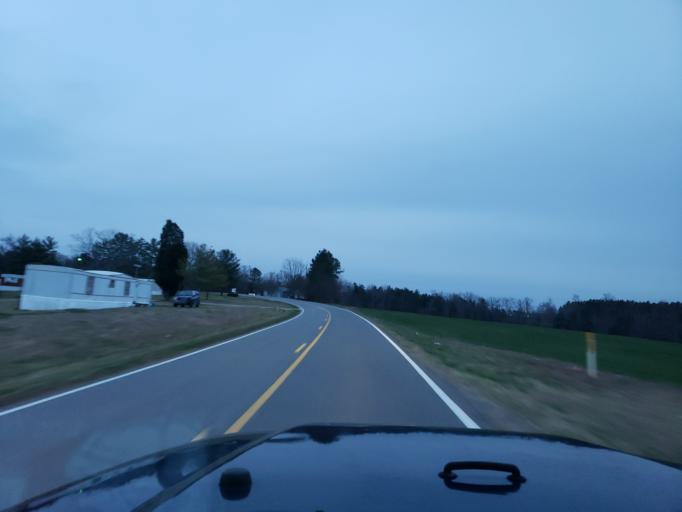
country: US
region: North Carolina
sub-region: Cleveland County
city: White Plains
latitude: 35.1858
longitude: -81.4307
